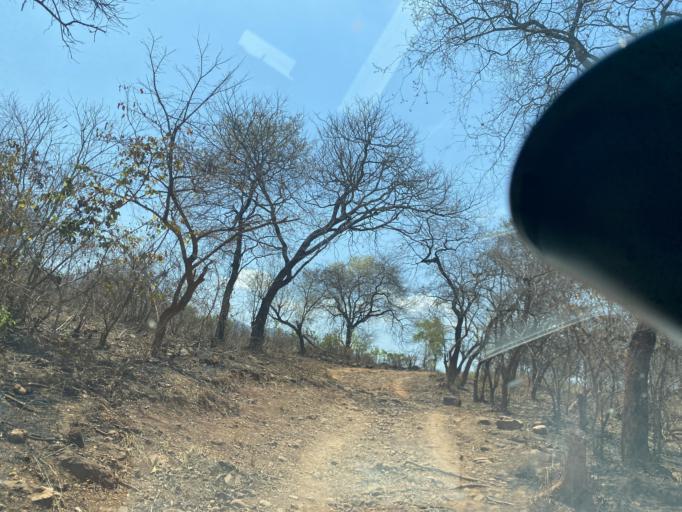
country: ZM
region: Lusaka
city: Kafue
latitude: -15.7839
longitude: 28.4606
